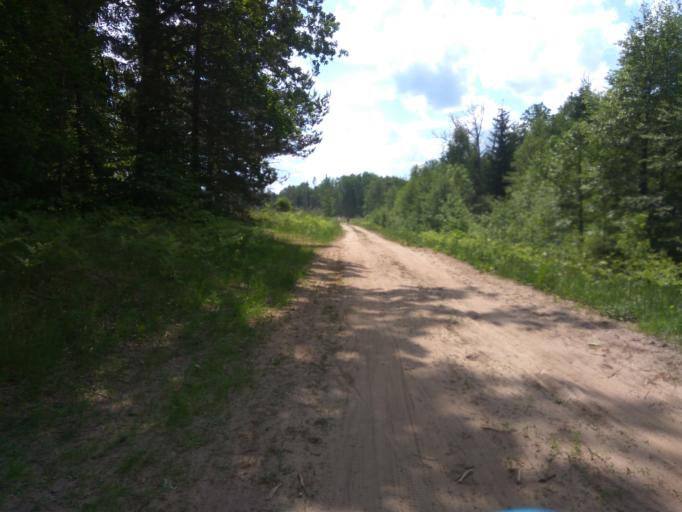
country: LV
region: Kuldigas Rajons
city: Kuldiga
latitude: 56.8843
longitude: 21.9728
